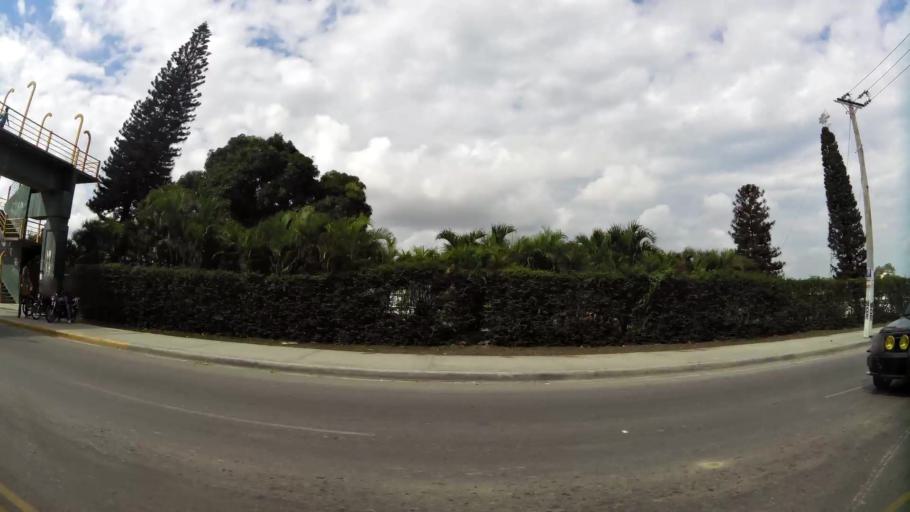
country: DO
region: Santiago
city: Santiago de los Caballeros
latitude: 19.4733
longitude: -70.7203
